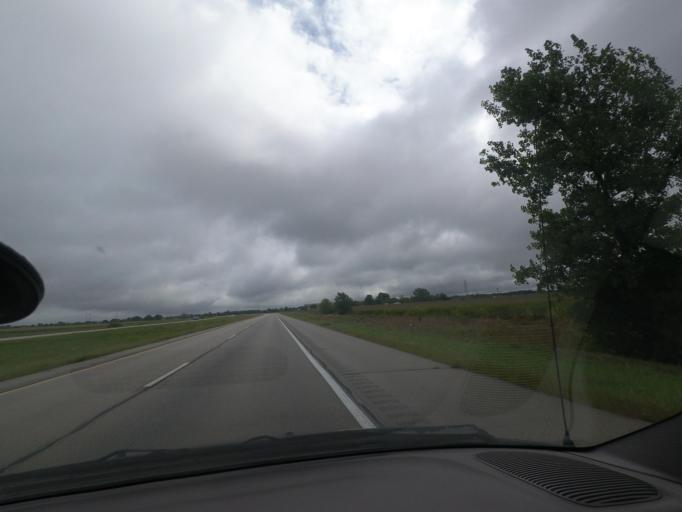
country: US
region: Illinois
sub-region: Piatt County
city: Monticello
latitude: 40.0310
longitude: -88.6120
